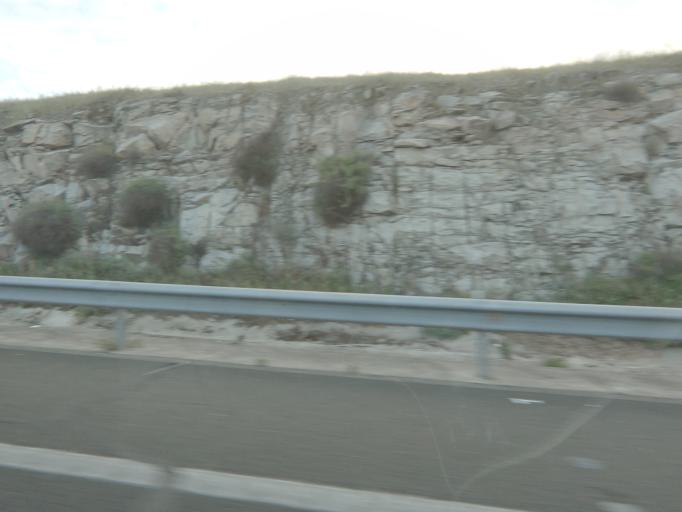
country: ES
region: Extremadura
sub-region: Provincia de Caceres
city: Caceres
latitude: 39.4460
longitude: -6.4132
